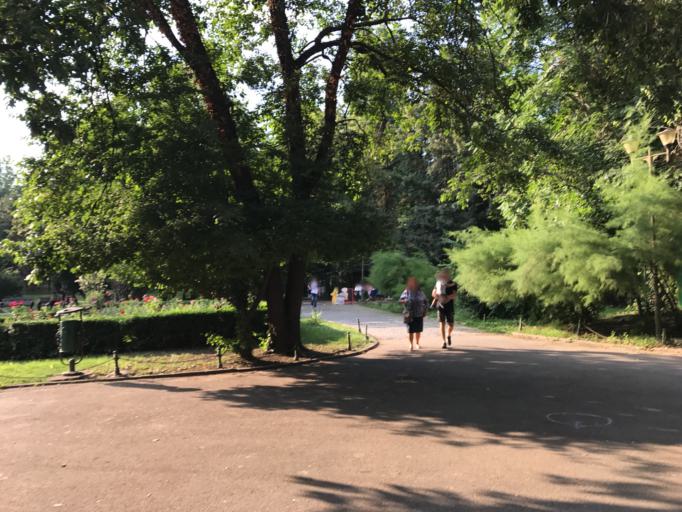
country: RO
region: Bucuresti
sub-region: Municipiul Bucuresti
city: Bucuresti
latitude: 44.4383
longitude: 26.0885
